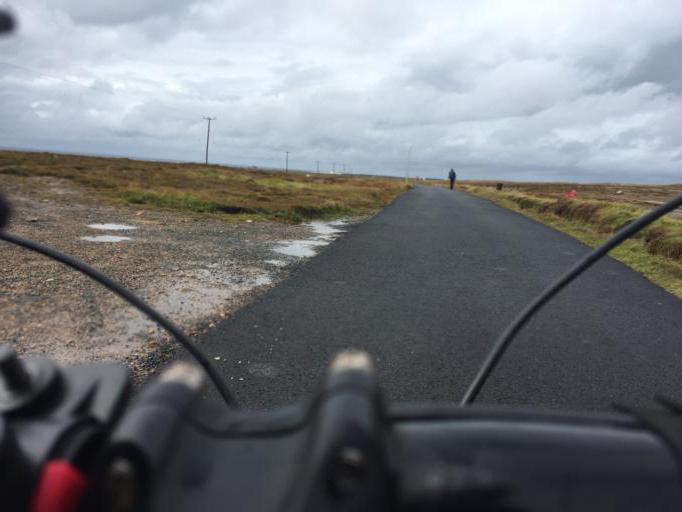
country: IE
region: Ulster
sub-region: County Donegal
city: Derrybeg
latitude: 55.2611
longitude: -8.2133
